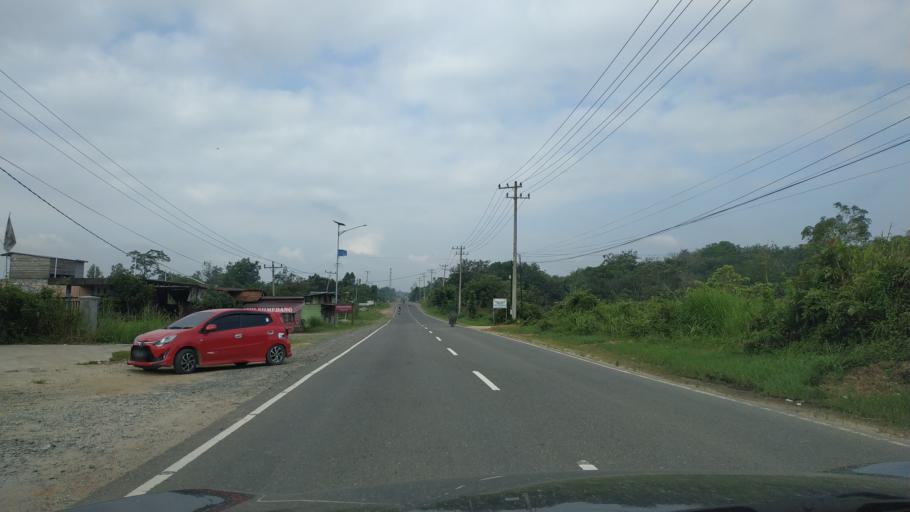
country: ID
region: Riau
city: Rengat
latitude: -0.3946
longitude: 102.4309
